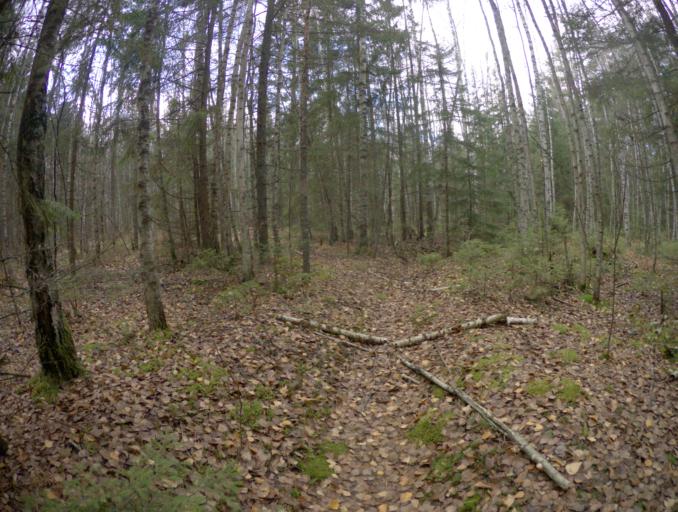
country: RU
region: Vladimir
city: Bogolyubovo
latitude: 56.0975
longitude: 40.5455
